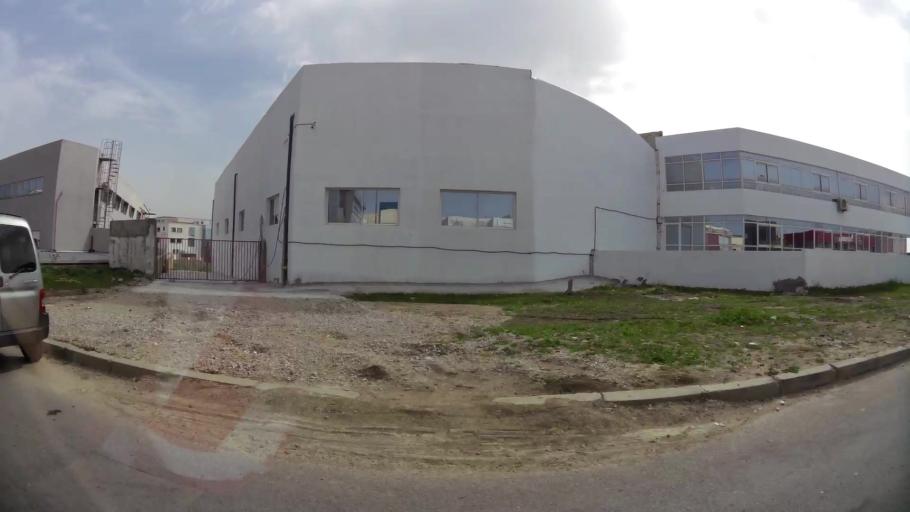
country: MA
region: Tanger-Tetouan
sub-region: Tanger-Assilah
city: Boukhalef
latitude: 35.7149
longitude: -5.8978
